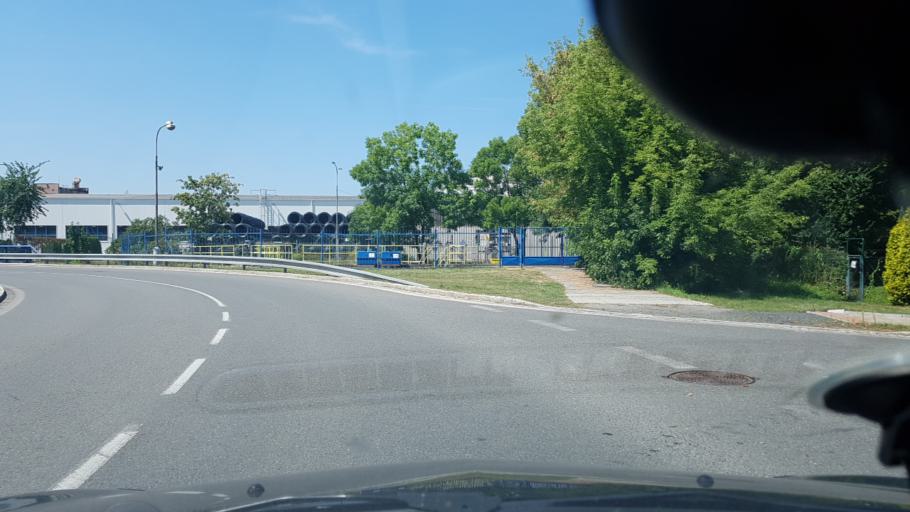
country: CZ
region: Moravskoslezsky
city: Bohumin
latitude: 49.8966
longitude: 18.3443
